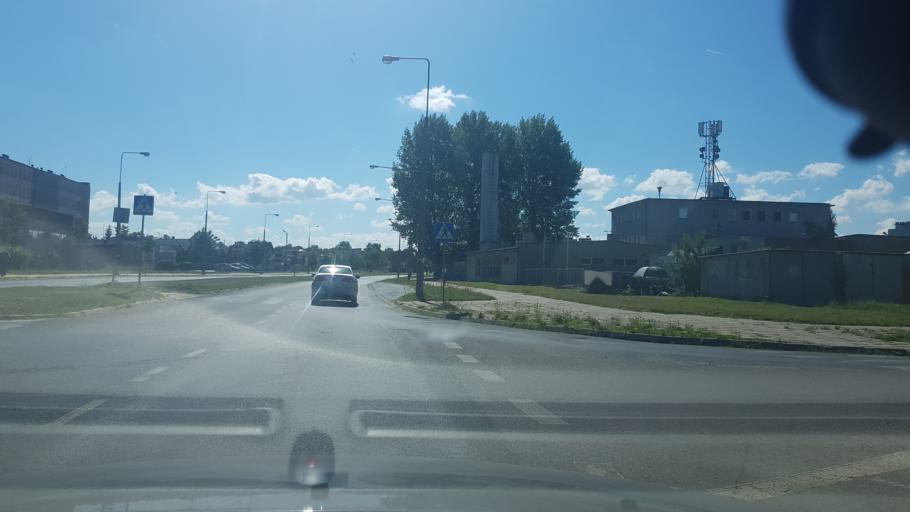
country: PL
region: Masovian Voivodeship
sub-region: Siedlce
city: Siedlce
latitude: 52.1780
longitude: 22.2761
